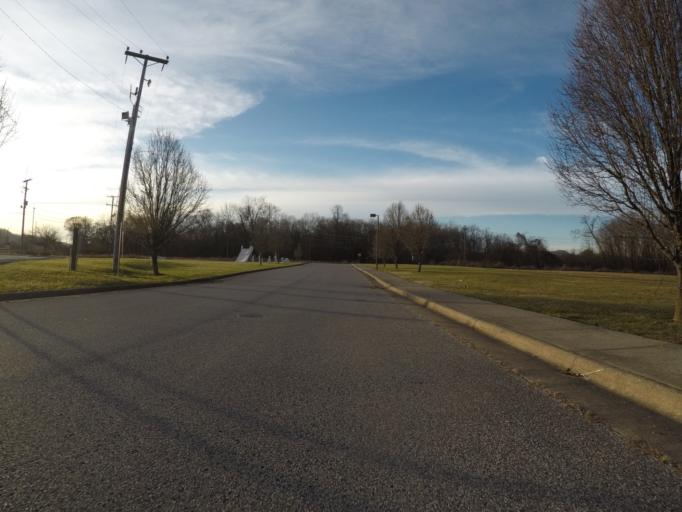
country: US
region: Ohio
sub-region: Lawrence County
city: Burlington
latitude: 38.4030
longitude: -82.4912
